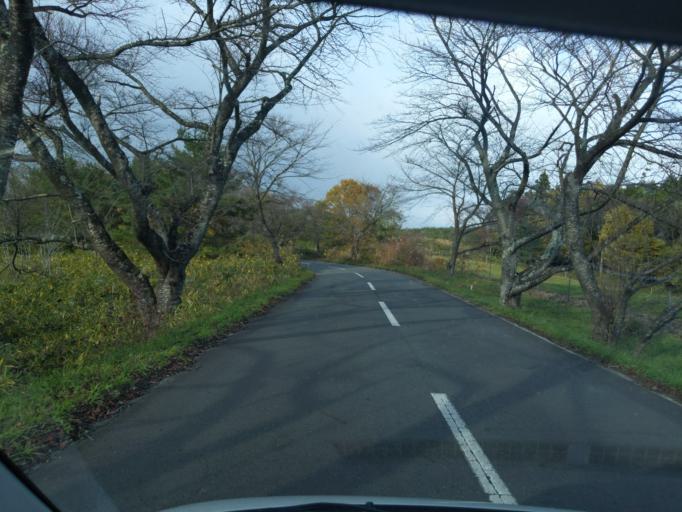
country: JP
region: Iwate
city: Mizusawa
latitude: 39.0398
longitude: 141.0794
